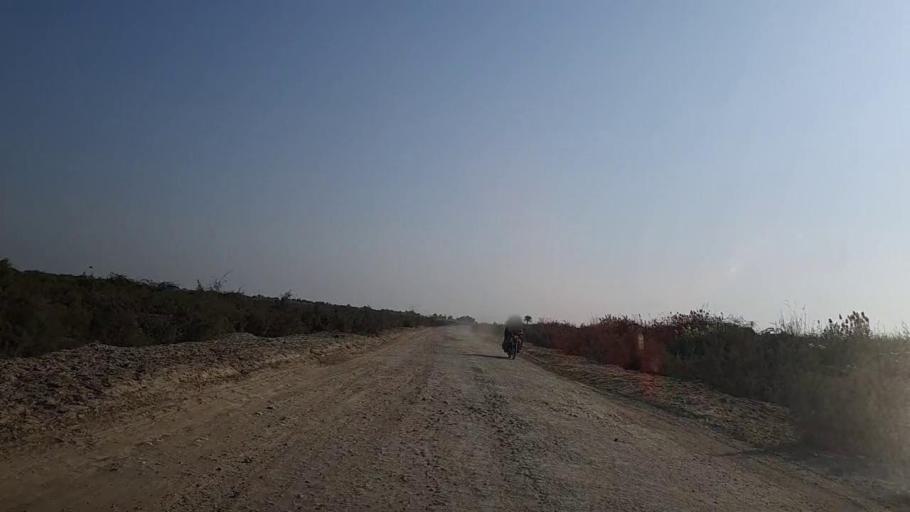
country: PK
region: Sindh
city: Tando Mittha Khan
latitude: 25.9078
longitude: 69.0766
